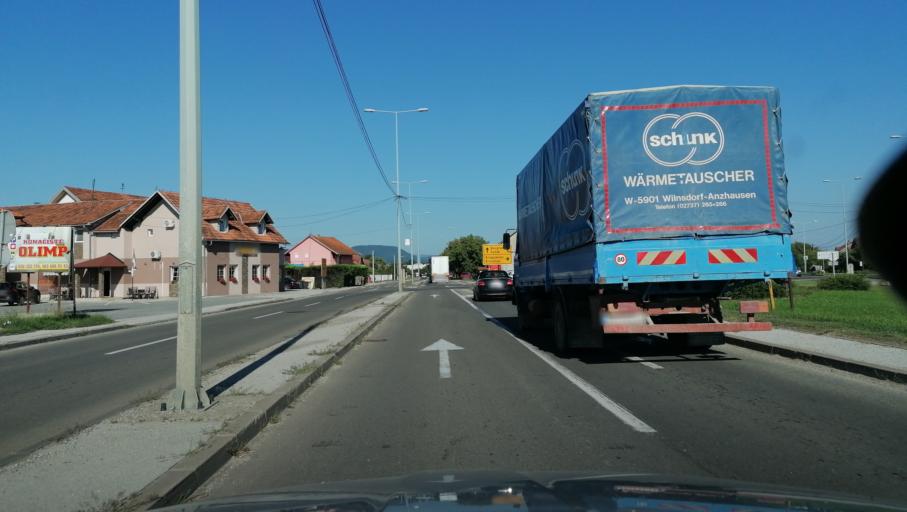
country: RS
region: Central Serbia
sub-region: Raski Okrug
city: Kraljevo
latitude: 43.7311
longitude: 20.6559
